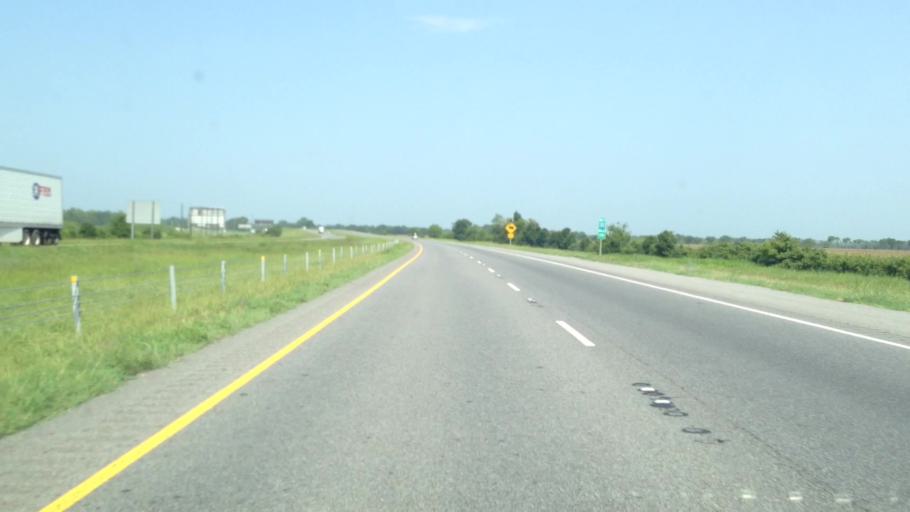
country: US
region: Louisiana
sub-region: Madison Parish
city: Tallulah
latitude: 32.4019
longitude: -91.2168
